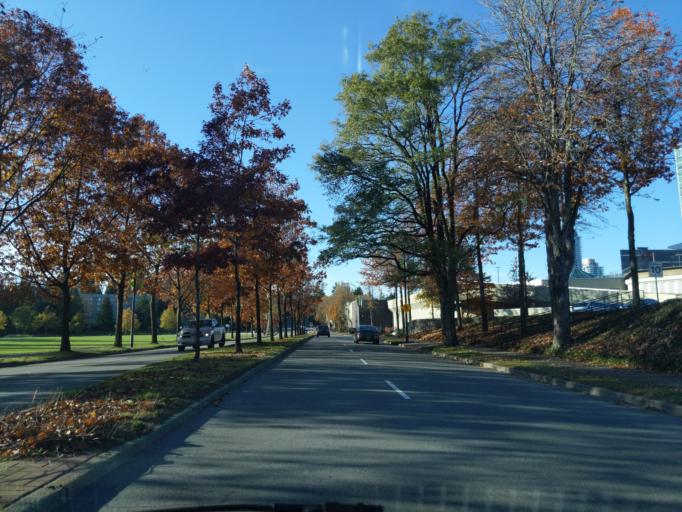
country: CA
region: British Columbia
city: New Westminster
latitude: 49.1846
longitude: -122.8480
